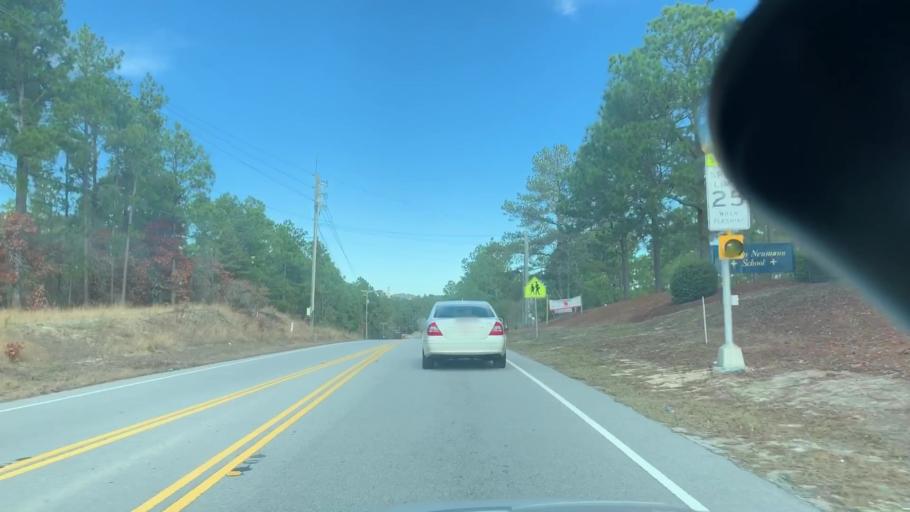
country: US
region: South Carolina
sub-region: Richland County
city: Woodfield
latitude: 34.0889
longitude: -80.8913
